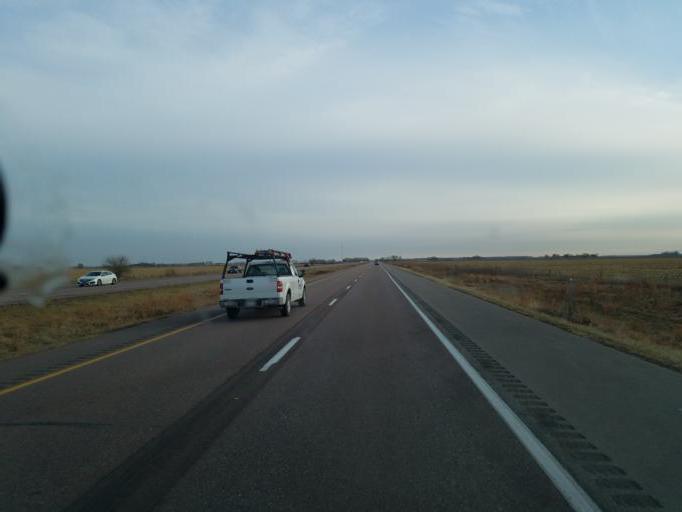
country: US
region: Iowa
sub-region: Monona County
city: Onawa
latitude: 42.1056
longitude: -96.1908
